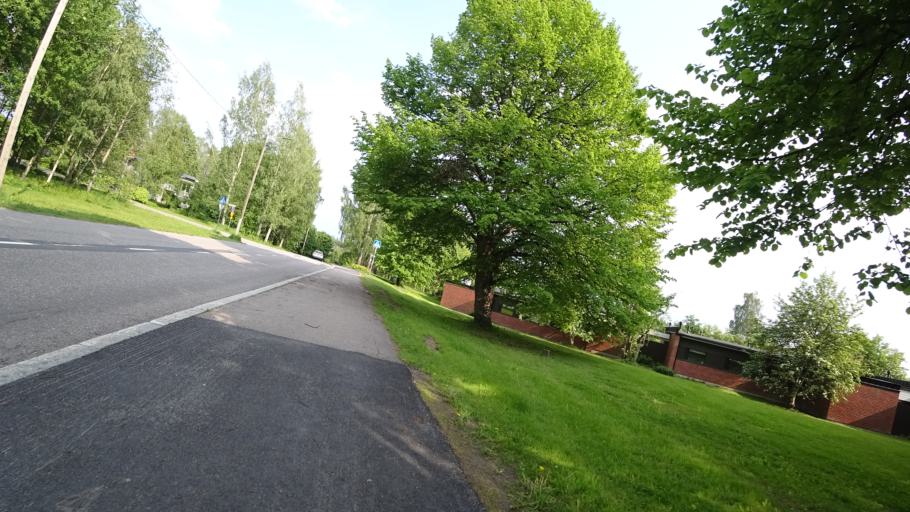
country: FI
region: Pirkanmaa
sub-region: Tampere
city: Pirkkala
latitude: 61.5019
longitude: 23.6642
